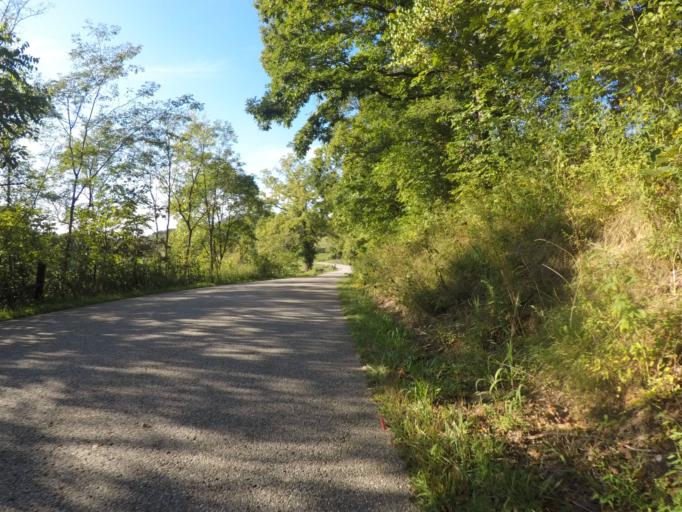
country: US
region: West Virginia
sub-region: Cabell County
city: Huntington
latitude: 38.5055
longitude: -82.4903
